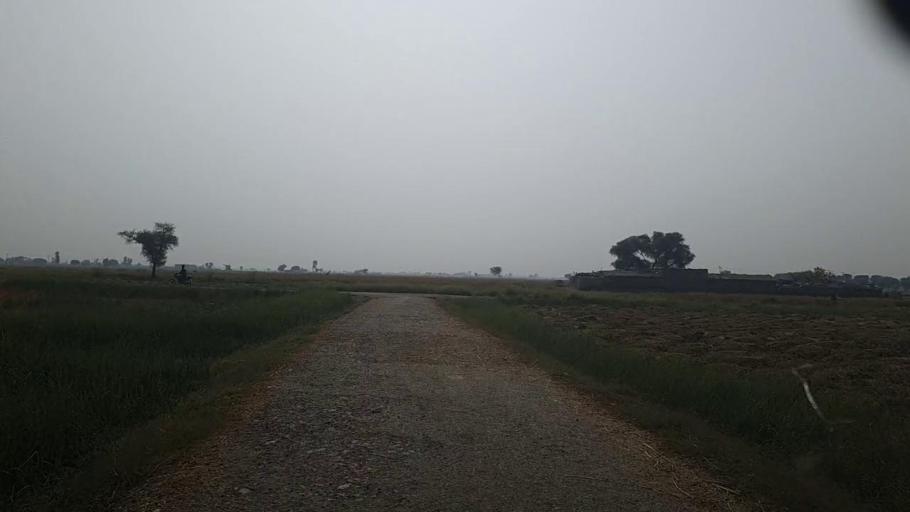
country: PK
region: Sindh
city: Kashmor
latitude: 28.3864
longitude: 69.4272
